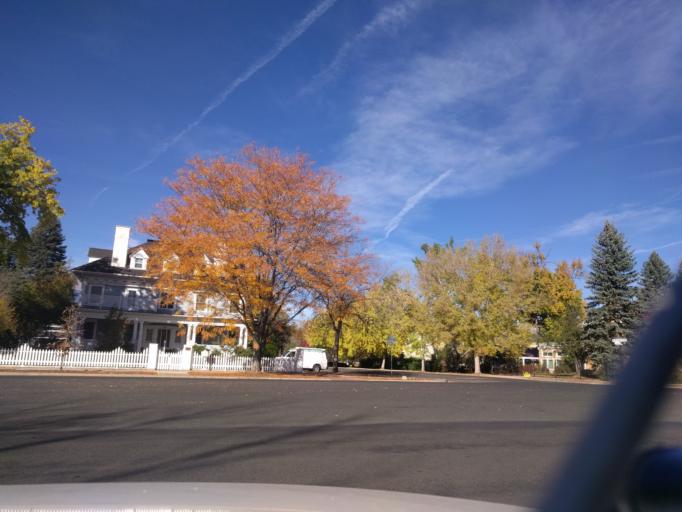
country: US
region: Colorado
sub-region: El Paso County
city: Colorado Springs
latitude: 38.8521
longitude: -104.8242
